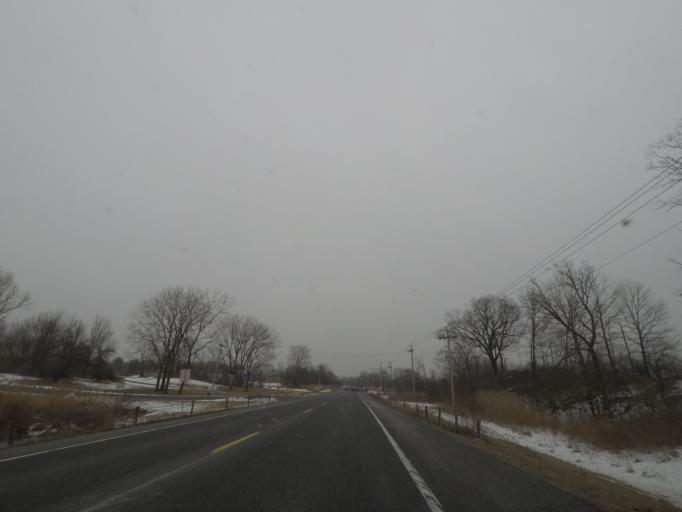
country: US
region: New York
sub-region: Albany County
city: Delmar
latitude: 42.5670
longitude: -73.8486
